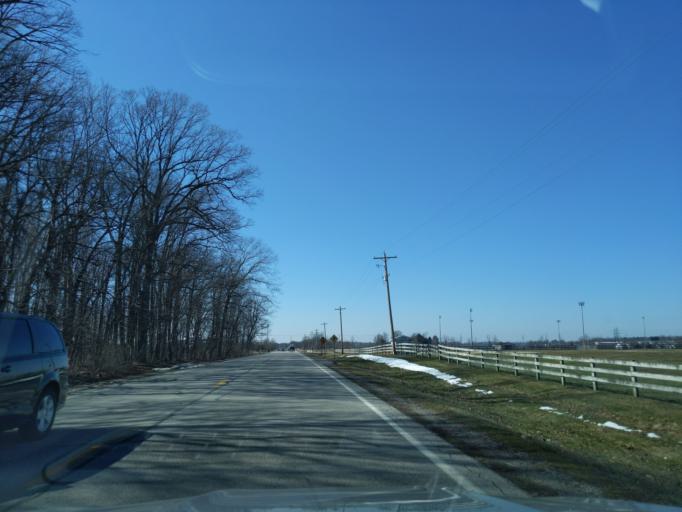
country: US
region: Indiana
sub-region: Tippecanoe County
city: West Lafayette
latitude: 40.4388
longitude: -86.9320
